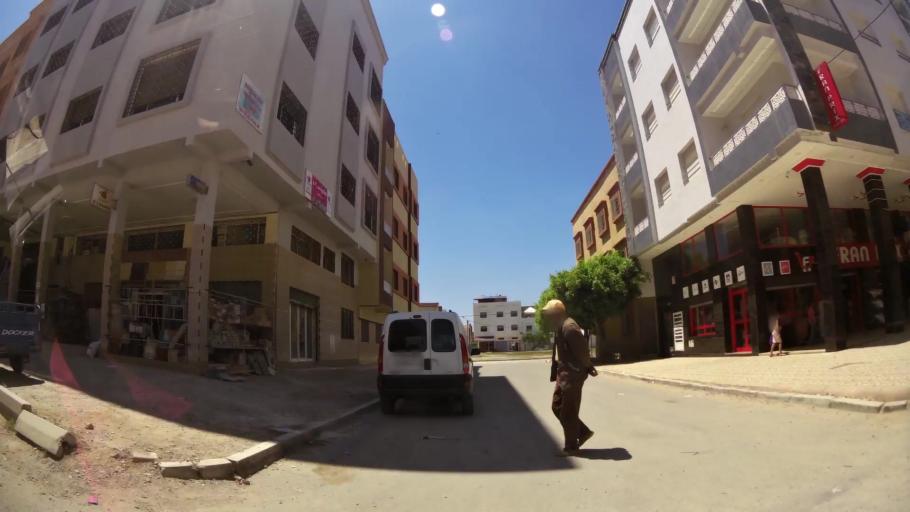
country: MA
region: Oriental
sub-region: Berkane-Taourirt
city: Madagh
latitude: 35.0769
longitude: -2.2237
